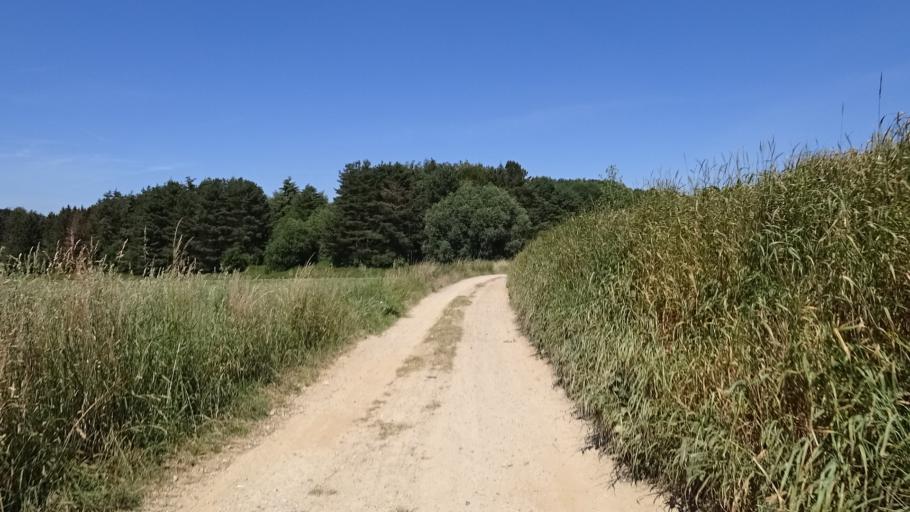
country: BE
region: Wallonia
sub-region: Province du Brabant Wallon
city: Jodoigne
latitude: 50.7086
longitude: 4.8662
